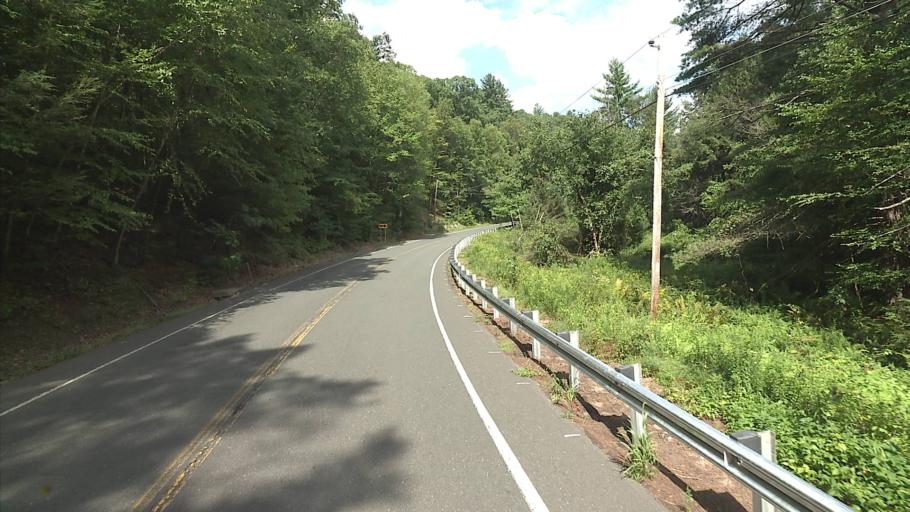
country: US
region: Massachusetts
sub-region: Hampden County
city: Granville
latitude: 42.0291
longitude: -72.8624
